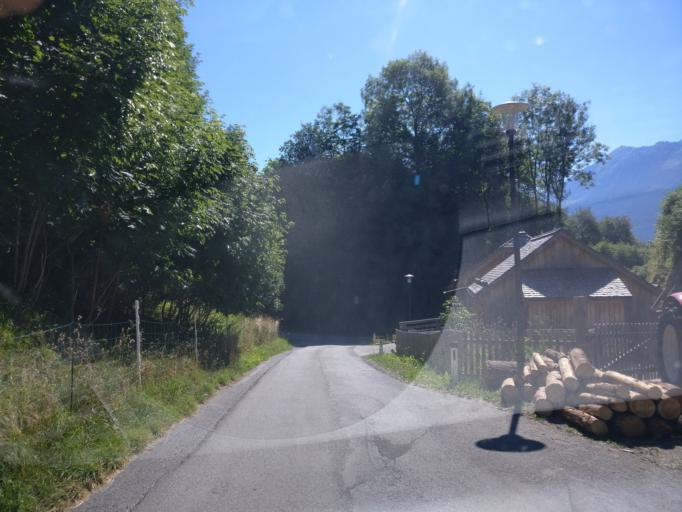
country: AT
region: Salzburg
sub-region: Politischer Bezirk Sankt Johann im Pongau
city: Goldegg
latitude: 47.3171
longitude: 13.0871
